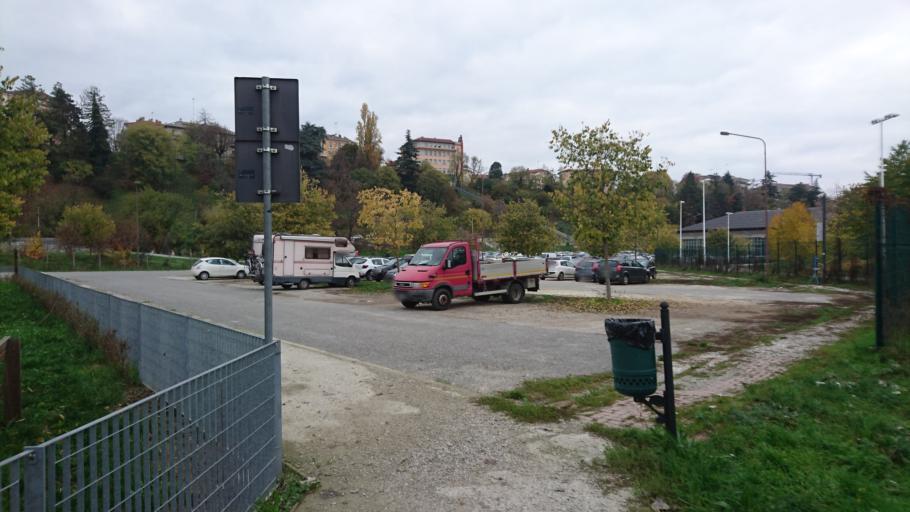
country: IT
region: Piedmont
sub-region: Provincia di Cuneo
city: Cuneo
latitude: 44.3856
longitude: 7.5522
